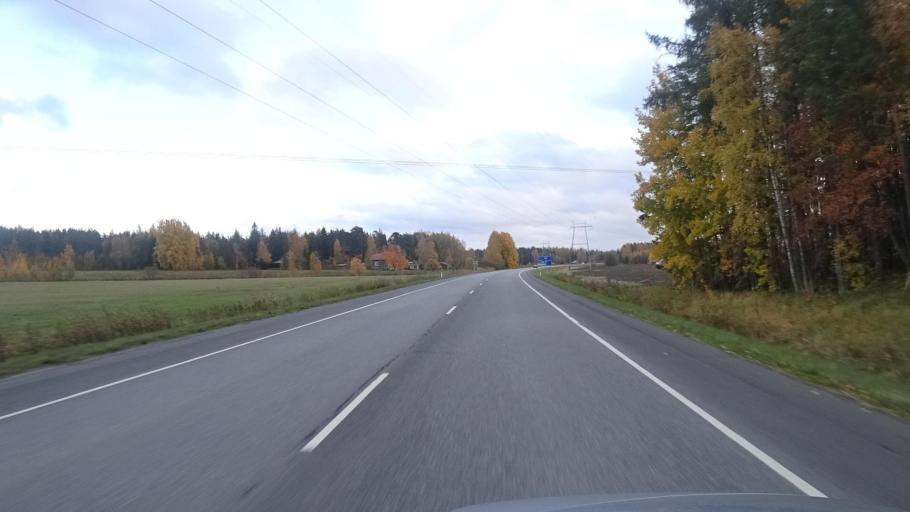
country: FI
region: Satakunta
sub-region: Rauma
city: Saekylae
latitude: 61.0251
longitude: 22.4044
